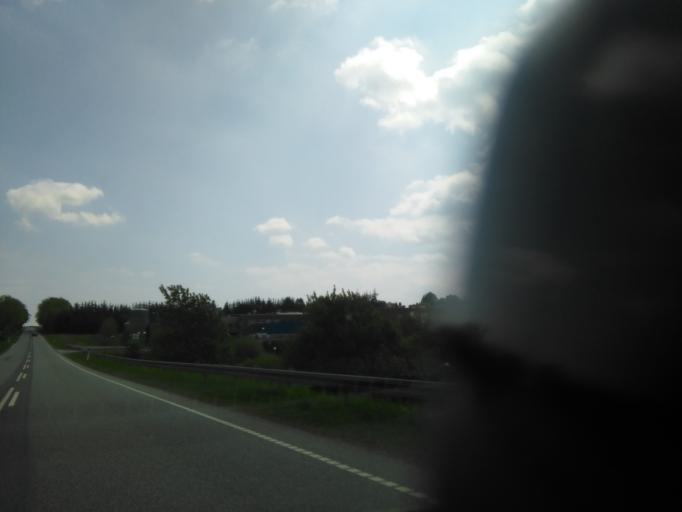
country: DK
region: Central Jutland
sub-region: Skanderborg Kommune
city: Stilling
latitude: 55.9916
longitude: 10.0240
